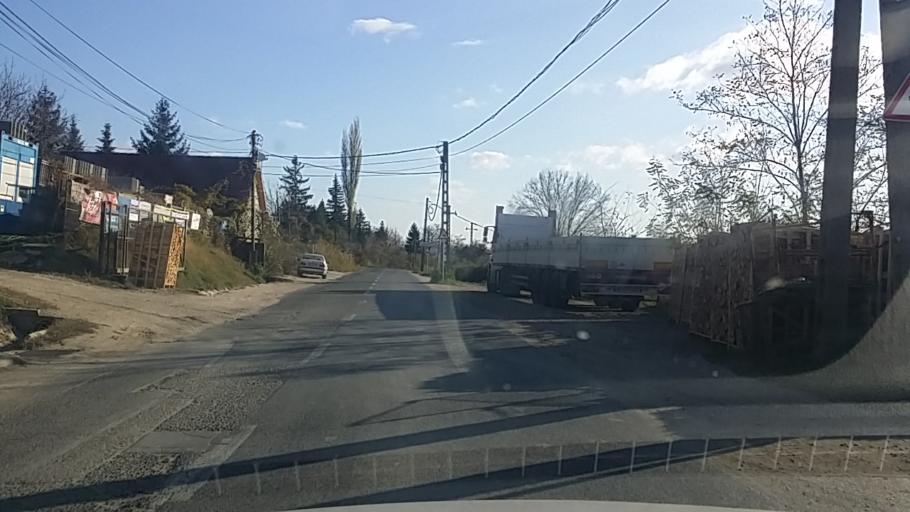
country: HU
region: Pest
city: Pilisszanto
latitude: 47.6623
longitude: 18.8940
